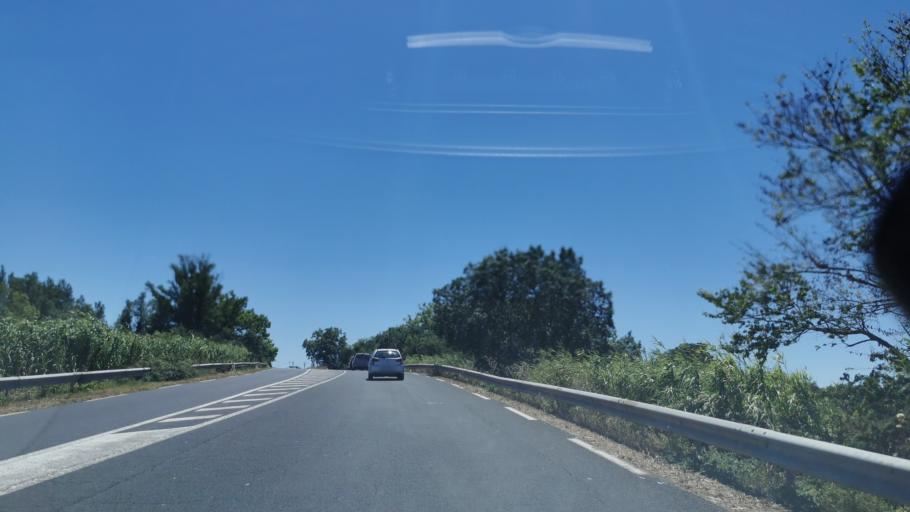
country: FR
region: Languedoc-Roussillon
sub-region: Departement de l'Herault
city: Beziers
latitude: 43.3319
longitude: 3.1944
